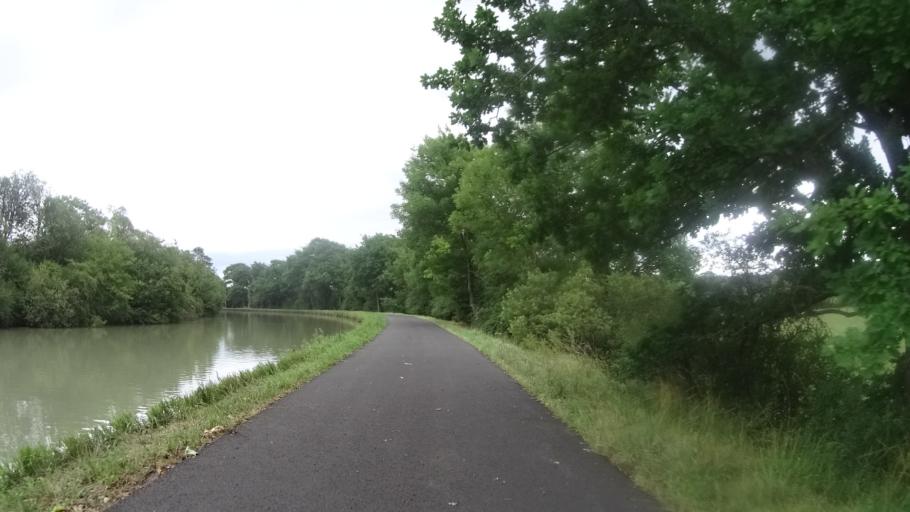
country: FR
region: Lorraine
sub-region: Departement de Meurthe-et-Moselle
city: Chanteheux
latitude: 48.6833
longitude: 6.6400
